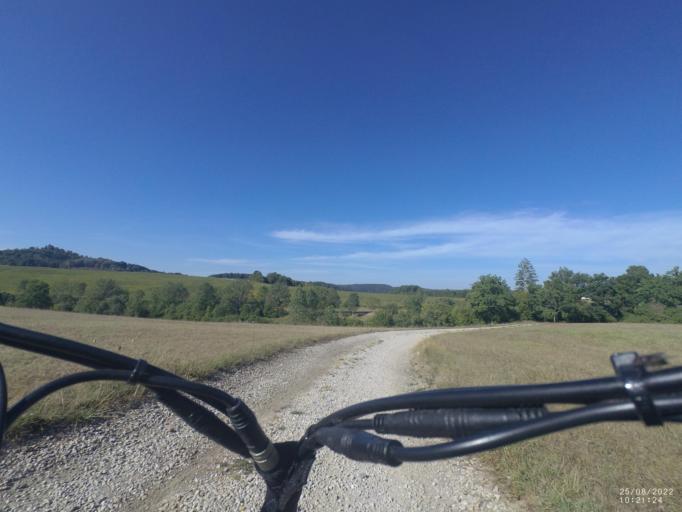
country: DE
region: Rheinland-Pfalz
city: Rockeskyll
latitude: 50.2653
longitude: 6.6889
